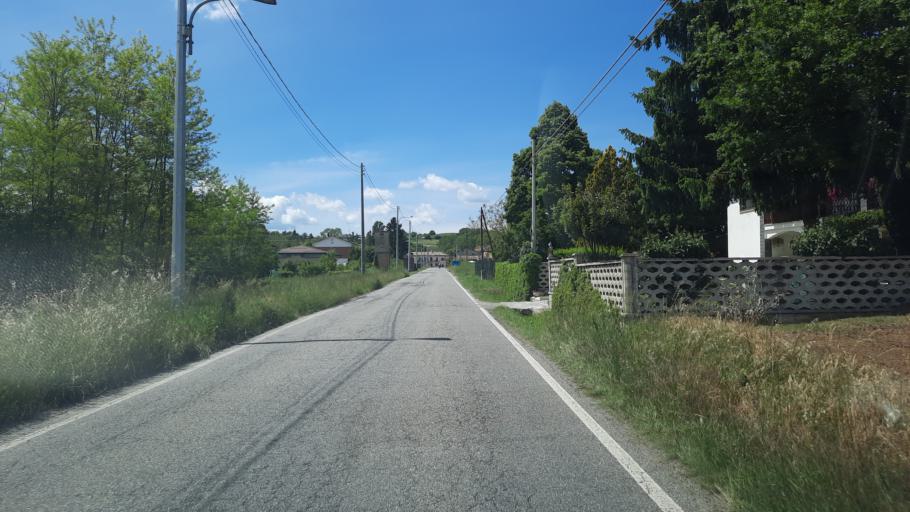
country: IT
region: Piedmont
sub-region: Provincia di Alessandria
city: Castelletto Merli
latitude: 45.0640
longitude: 8.2469
